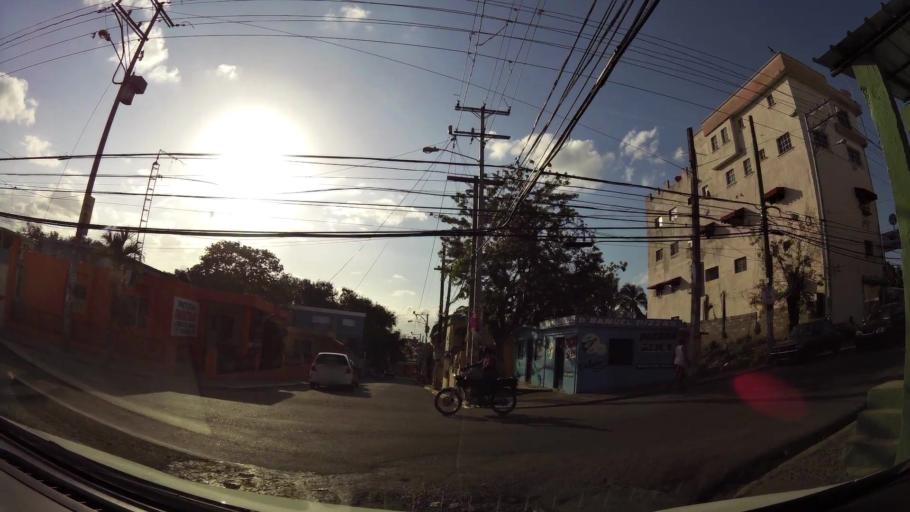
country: DO
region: Nacional
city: Ensanche Luperon
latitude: 18.5445
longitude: -69.9053
